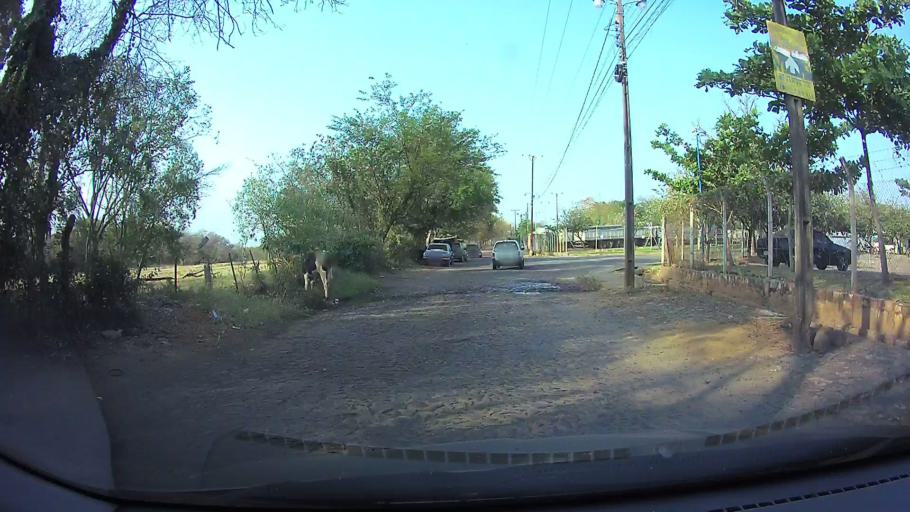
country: PY
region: Central
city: Limpio
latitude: -25.2254
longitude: -57.5081
